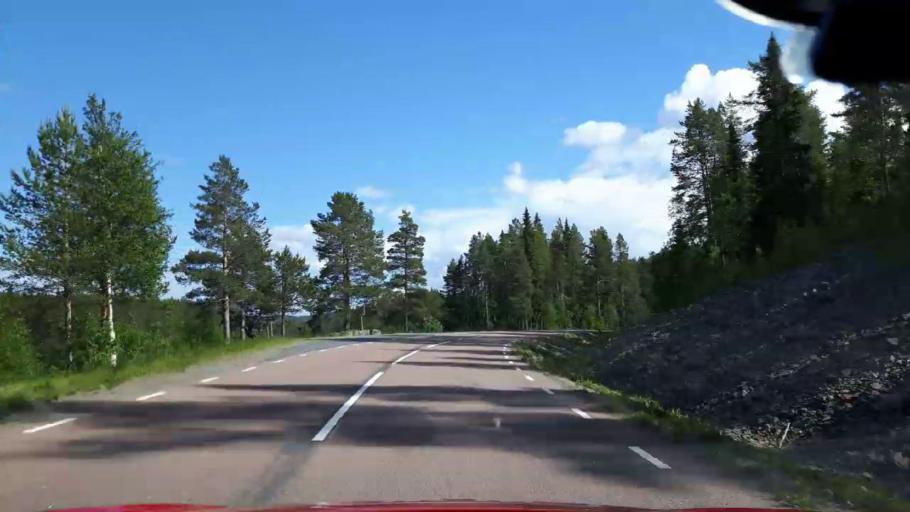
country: SE
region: Jaemtland
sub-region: Krokoms Kommun
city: Valla
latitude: 64.0105
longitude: 14.2309
